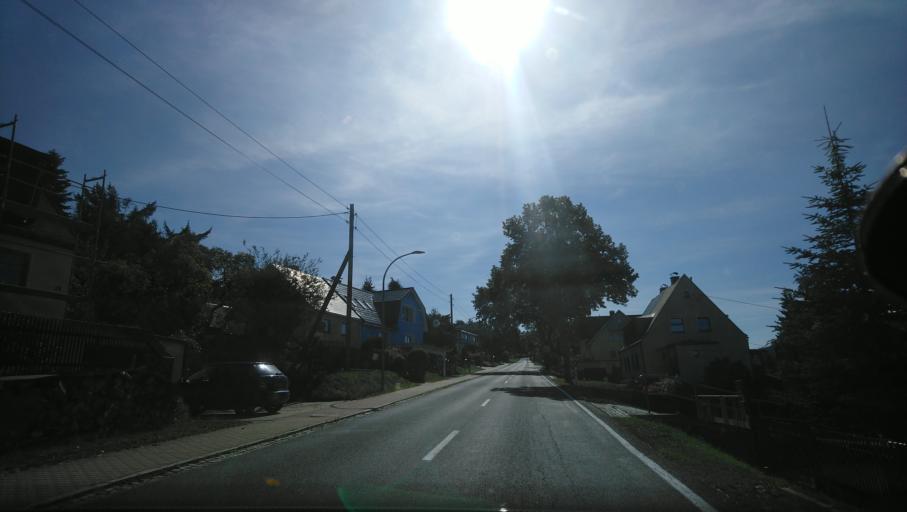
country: DE
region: Saxony
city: Konigswalde
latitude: 50.5405
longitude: 13.0544
